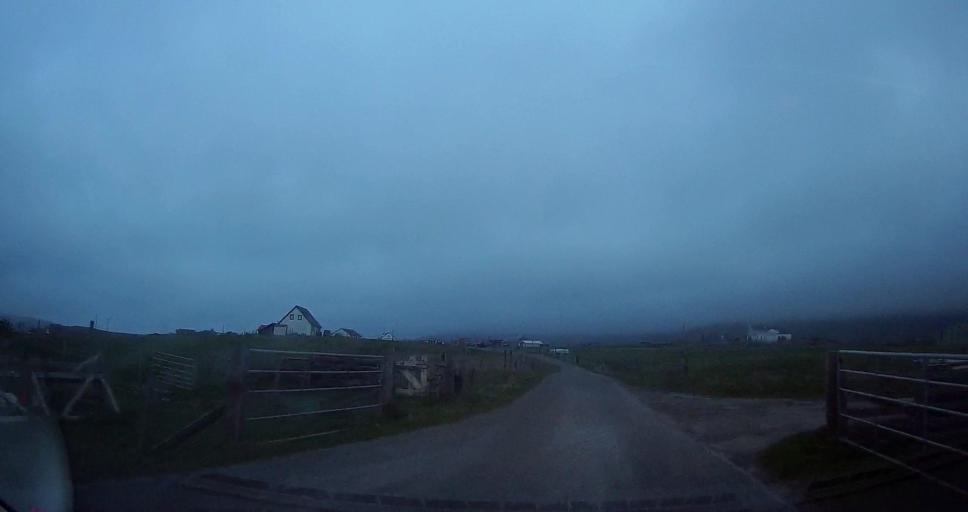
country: GB
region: Scotland
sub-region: Shetland Islands
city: Sandwick
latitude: 60.0418
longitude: -1.2177
